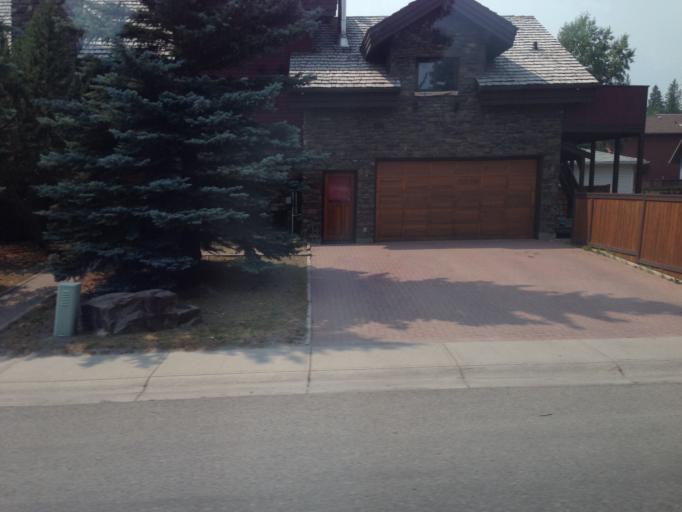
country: CA
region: Alberta
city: Canmore
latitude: 51.0954
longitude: -115.3589
